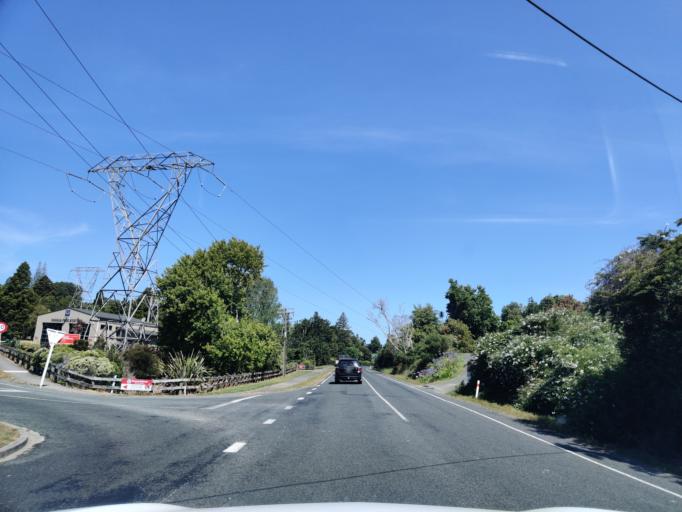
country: NZ
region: Auckland
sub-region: Auckland
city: Red Hill
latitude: -37.0782
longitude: 175.0705
